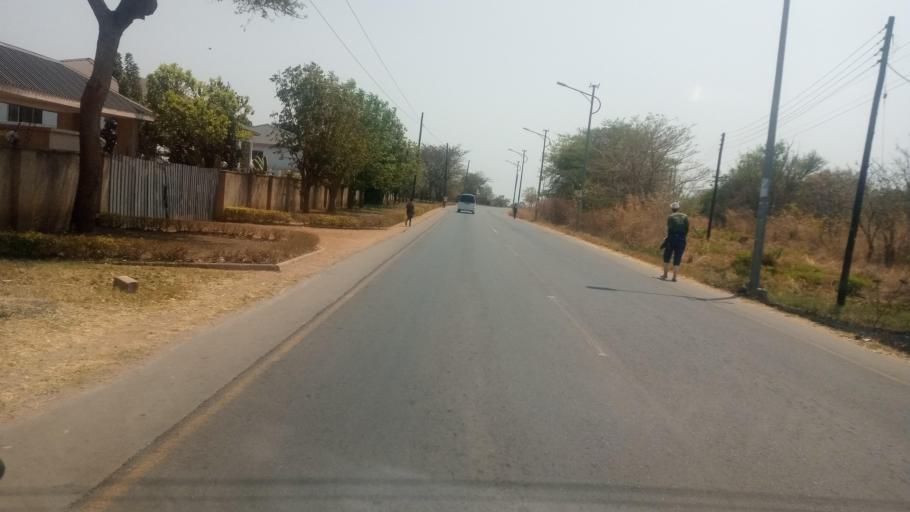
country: ZM
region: Lusaka
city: Lusaka
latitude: -15.4784
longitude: 28.4187
